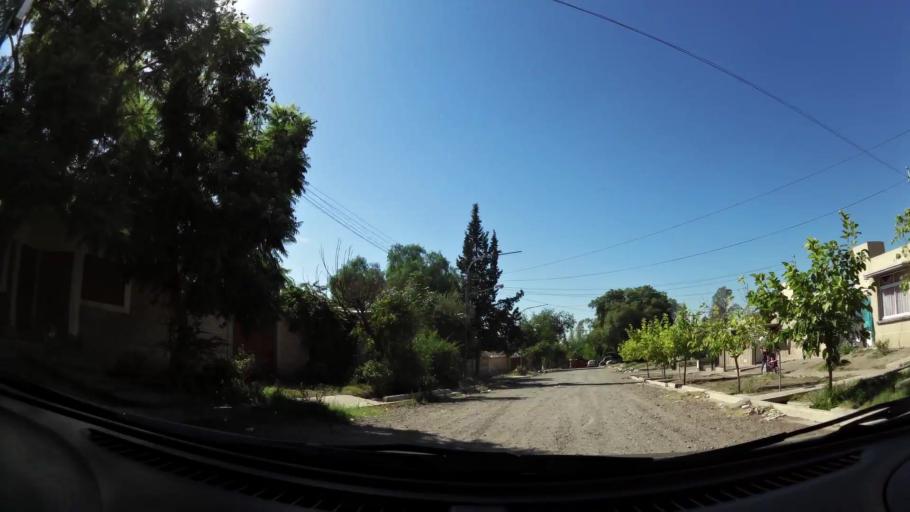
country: AR
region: Mendoza
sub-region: Departamento de Godoy Cruz
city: Godoy Cruz
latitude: -32.9066
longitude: -68.8808
